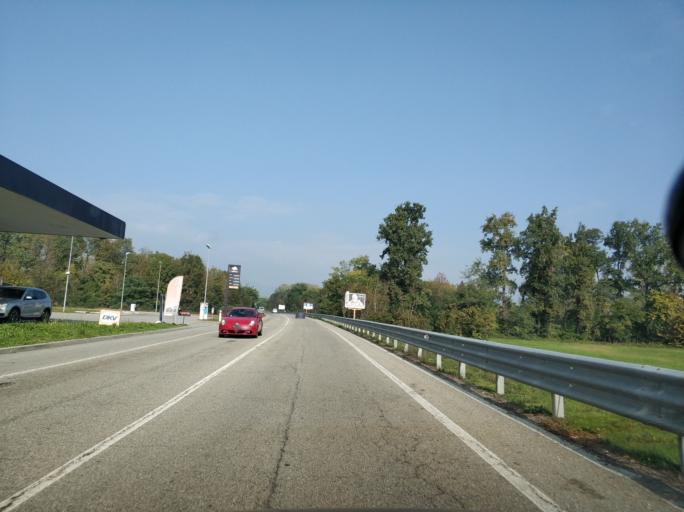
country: IT
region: Piedmont
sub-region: Provincia di Biella
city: Ponderano
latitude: 45.5313
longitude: 8.0419
